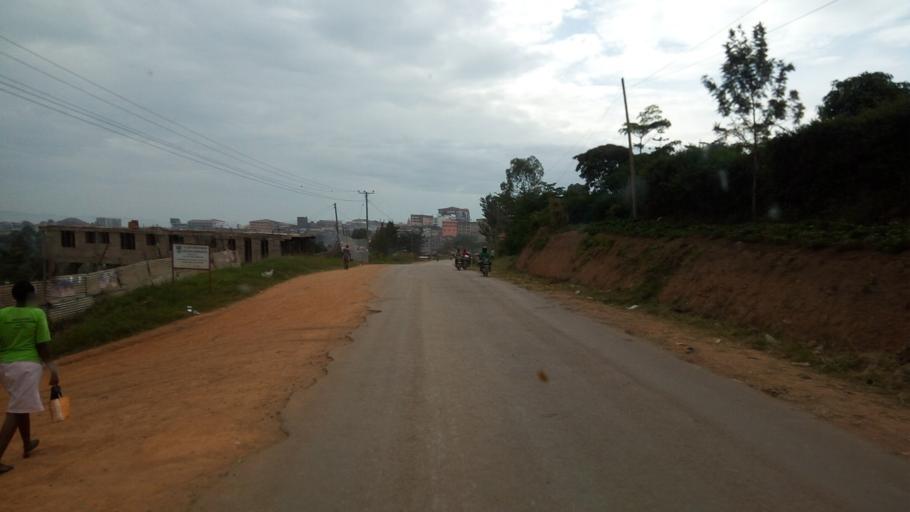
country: UG
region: Western Region
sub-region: Mbarara District
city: Mbarara
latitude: -0.6051
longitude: 30.6549
